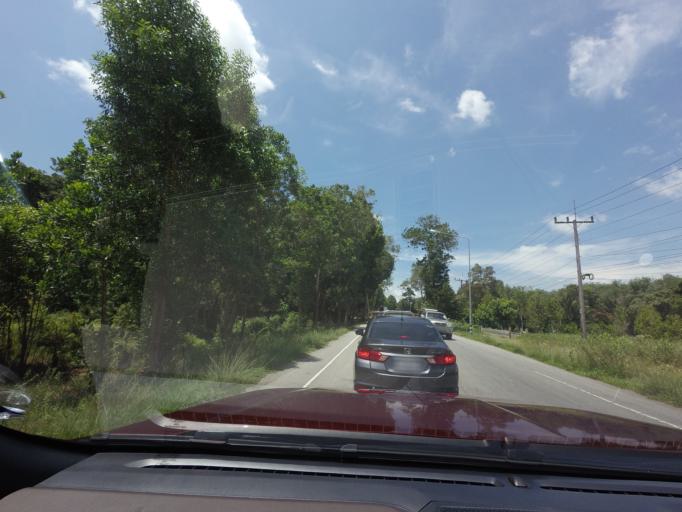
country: TH
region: Narathiwat
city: Ra-ngae
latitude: 6.2272
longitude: 101.6796
